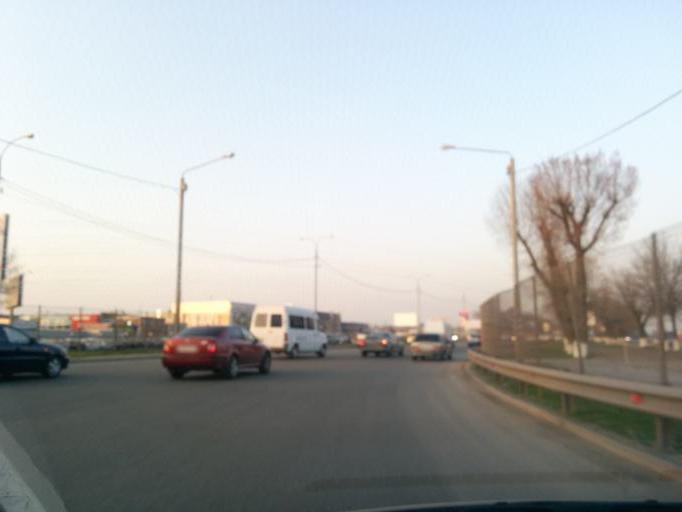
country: RU
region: Rostov
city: Aksay
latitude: 47.2726
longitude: 39.8256
